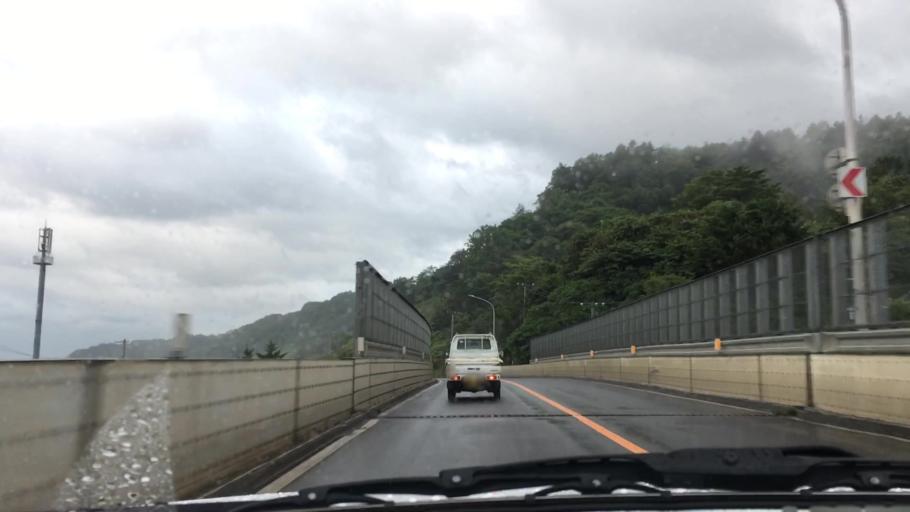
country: JP
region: Hokkaido
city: Nanae
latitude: 42.1283
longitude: 140.5150
